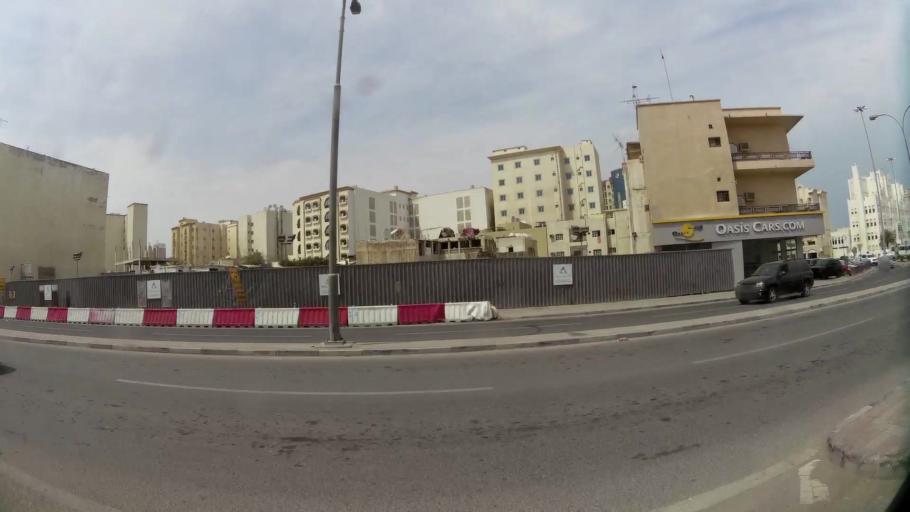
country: QA
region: Baladiyat ad Dawhah
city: Doha
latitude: 25.2755
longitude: 51.5386
